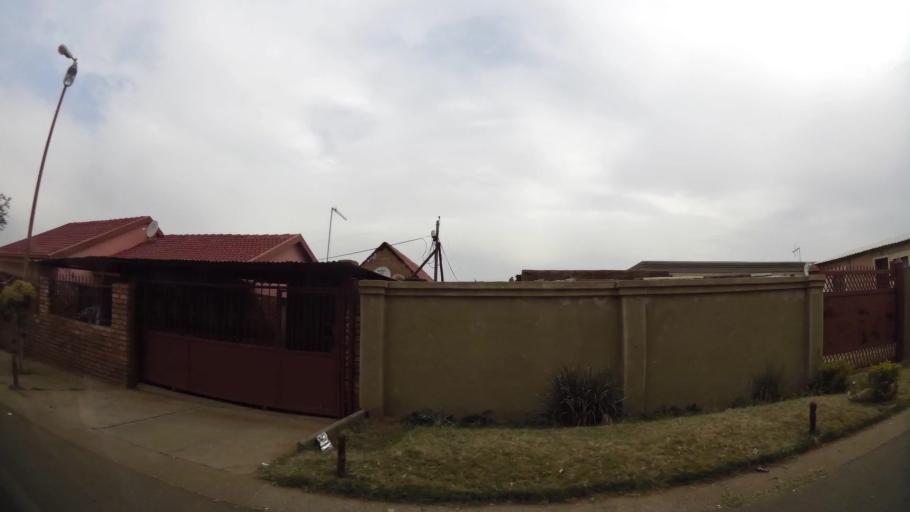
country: ZA
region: Gauteng
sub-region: City of Tshwane Metropolitan Municipality
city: Pretoria
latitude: -25.7057
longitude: 28.3445
